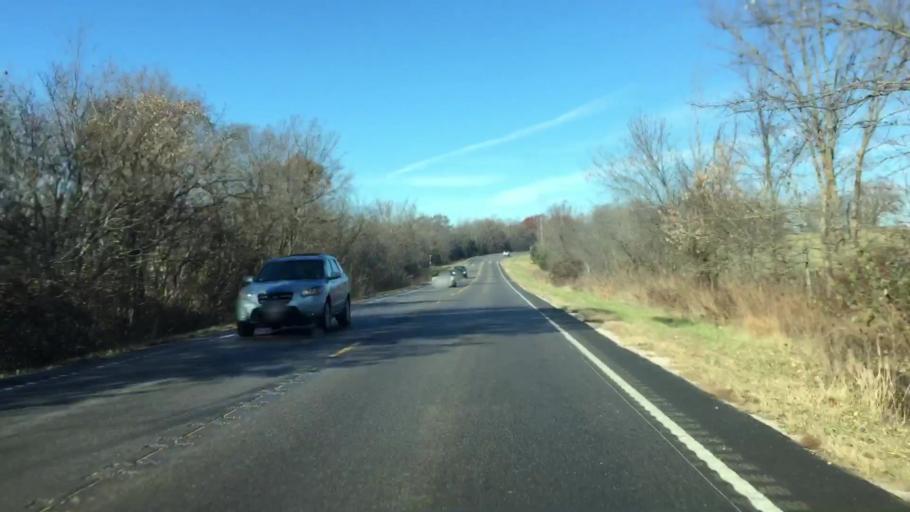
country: US
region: Missouri
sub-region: Miller County
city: Eldon
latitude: 38.3635
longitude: -92.6109
